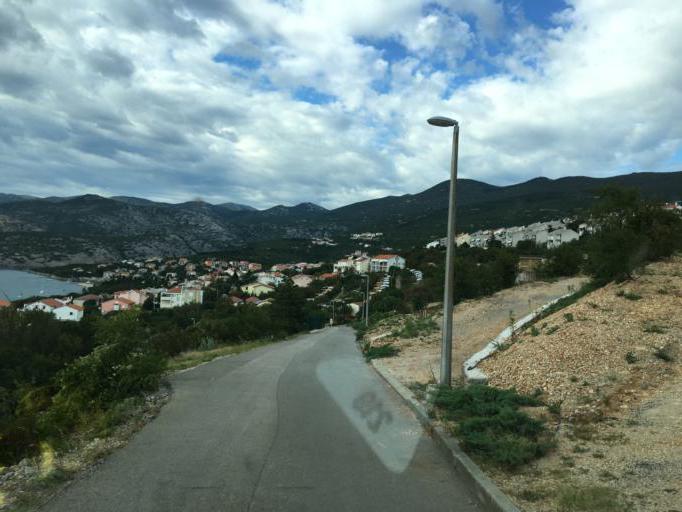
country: HR
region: Primorsko-Goranska
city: Novi Vinodolski
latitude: 45.0967
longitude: 14.8443
